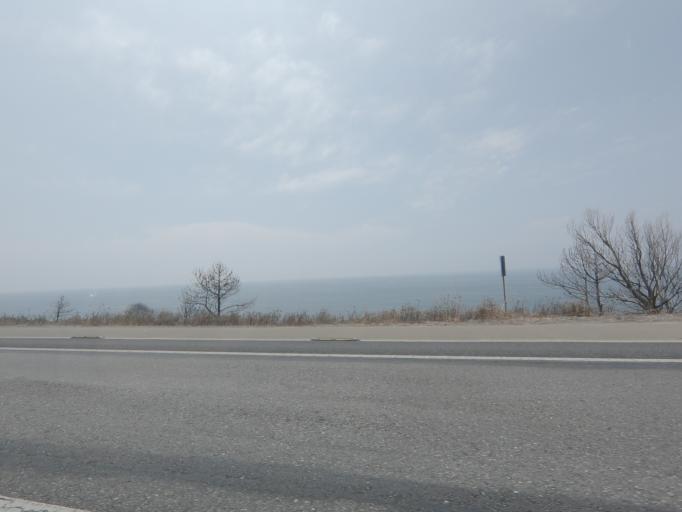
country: ES
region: Galicia
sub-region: Provincia de Pontevedra
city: A Guarda
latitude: 41.9358
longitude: -8.8844
